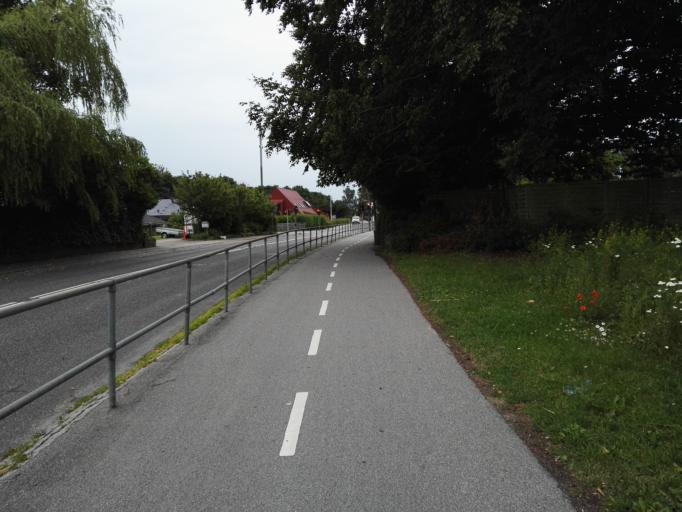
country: DK
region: Zealand
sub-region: Roskilde Kommune
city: Jyllinge
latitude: 55.7560
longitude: 12.1090
